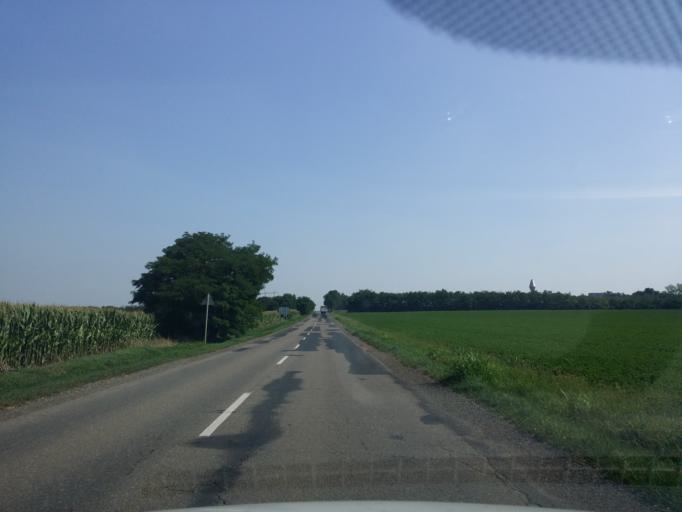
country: HU
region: Fejer
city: Mezofalva
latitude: 46.9486
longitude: 18.7408
